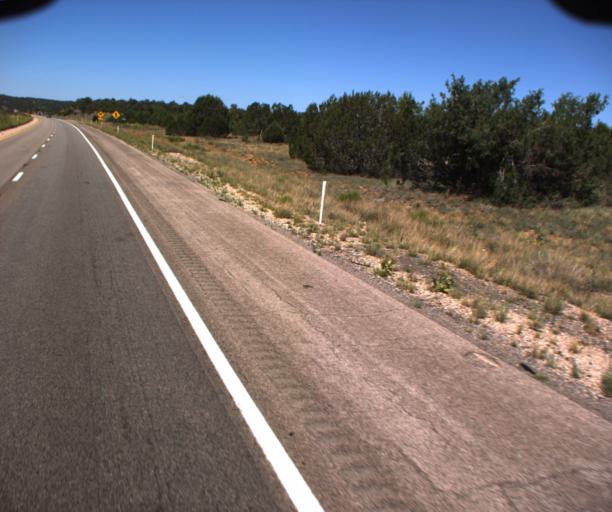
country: US
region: Arizona
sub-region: Mohave County
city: Peach Springs
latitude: 35.2892
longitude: -113.0884
